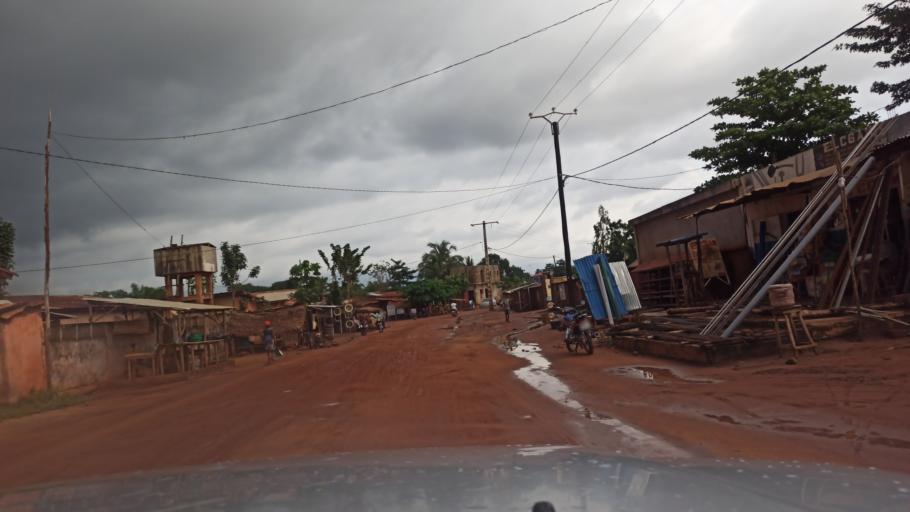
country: BJ
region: Queme
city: Porto-Novo
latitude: 6.5598
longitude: 2.5900
